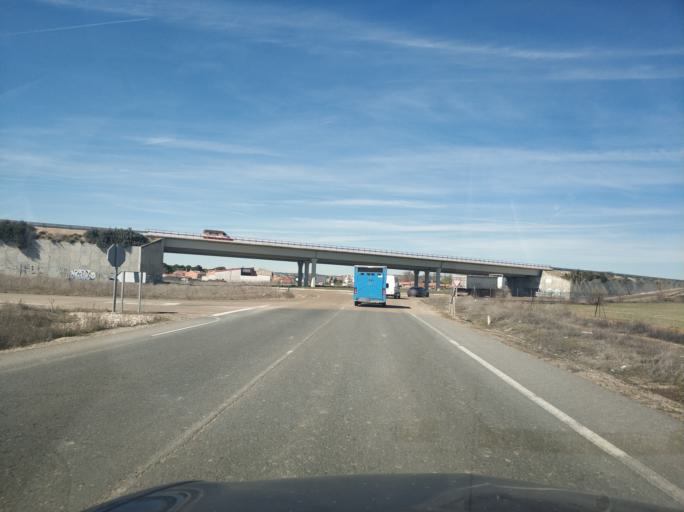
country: ES
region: Castille and Leon
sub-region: Provincia de Valladolid
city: Viana de Cega
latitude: 41.5480
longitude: -4.7866
